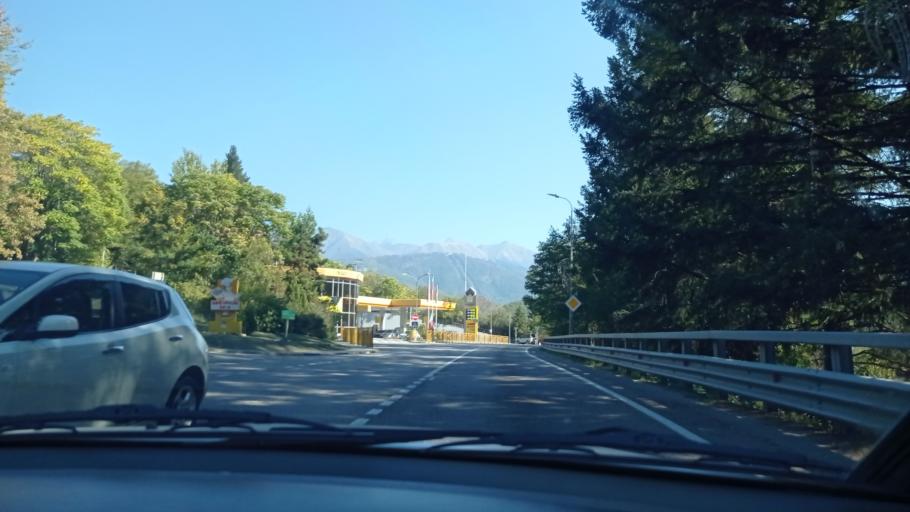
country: RU
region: Krasnodarskiy
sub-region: Sochi City
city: Krasnaya Polyana
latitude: 43.6824
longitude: 40.2197
